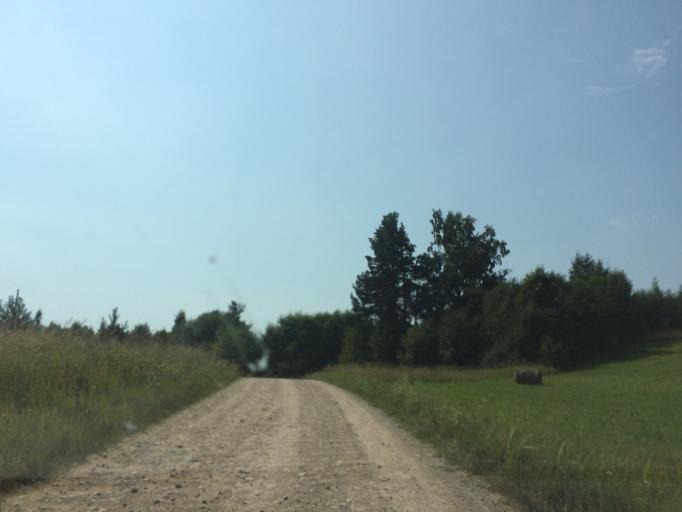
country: LV
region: Ludzas Rajons
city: Ludza
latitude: 56.5388
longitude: 27.5831
